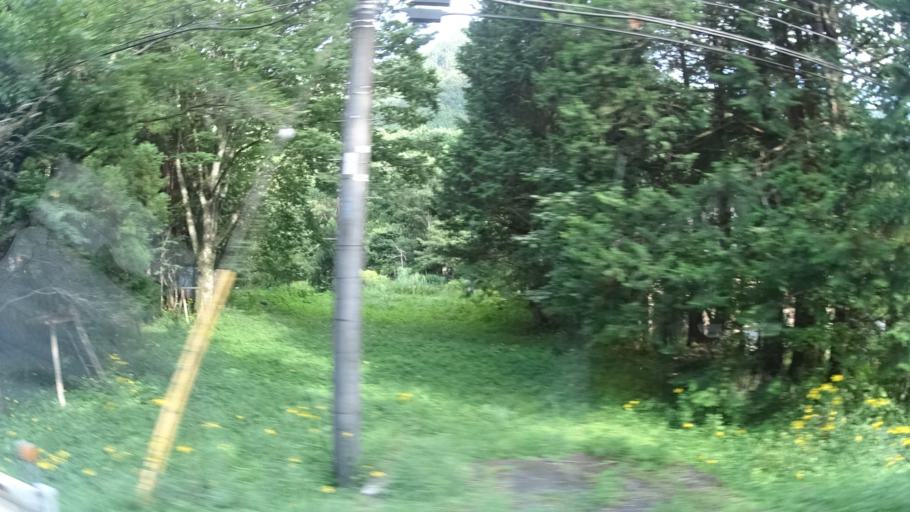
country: JP
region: Tochigi
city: Nikko
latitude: 36.6815
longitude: 139.4894
